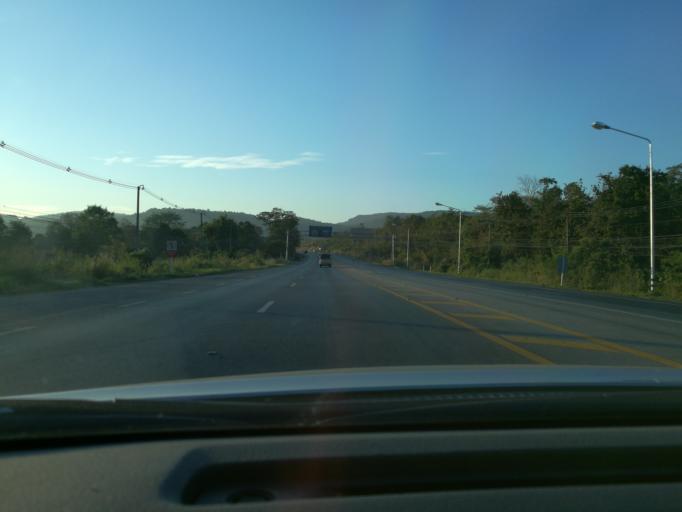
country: TH
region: Phitsanulok
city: Wang Thong
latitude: 16.8643
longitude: 100.4991
